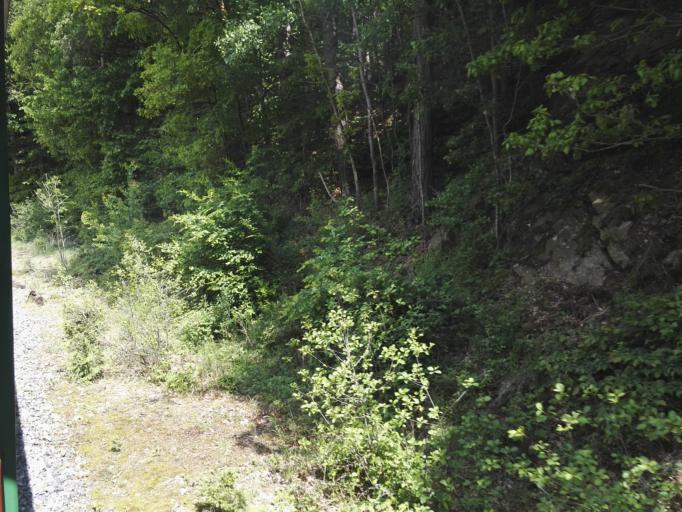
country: AT
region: Styria
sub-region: Politischer Bezirk Weiz
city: Baierdorf-Umgebung
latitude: 47.2650
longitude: 15.7093
